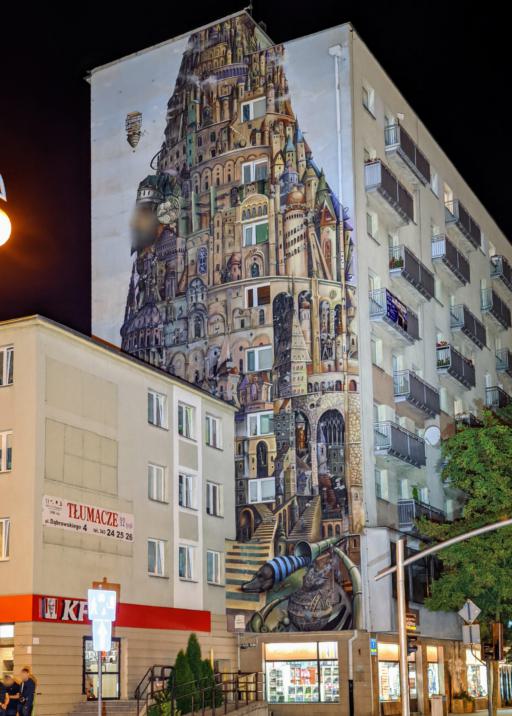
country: PL
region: Silesian Voivodeship
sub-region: Czestochowa
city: Czestochowa
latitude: 50.8120
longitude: 19.1125
